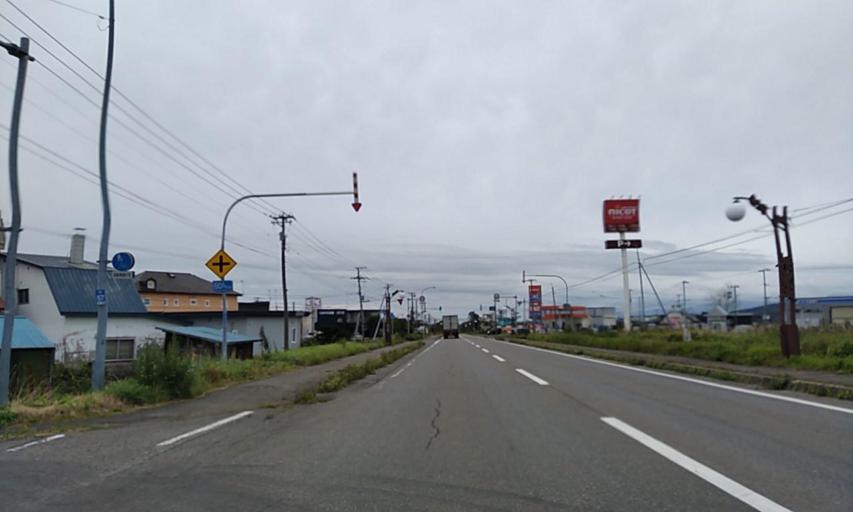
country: JP
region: Hokkaido
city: Obihiro
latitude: 42.4826
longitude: 143.2727
